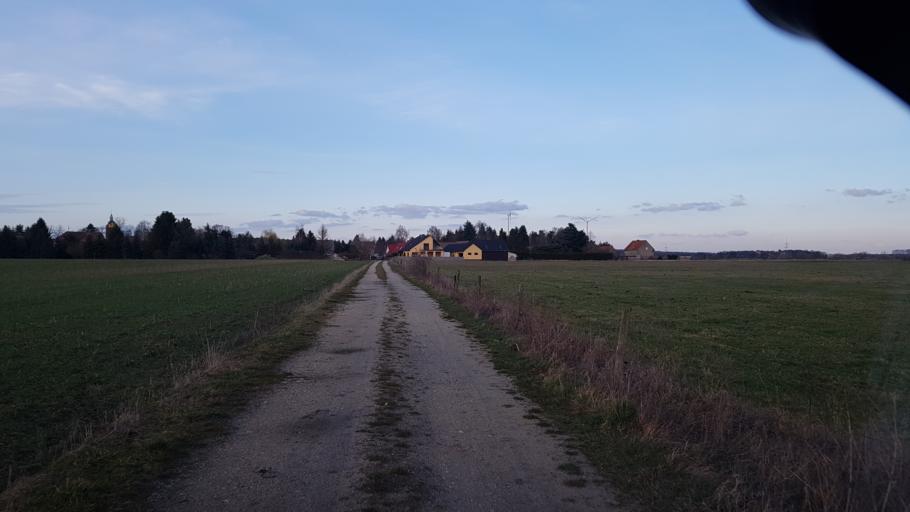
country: DE
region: Brandenburg
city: Schonborn
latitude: 51.5907
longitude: 13.5041
